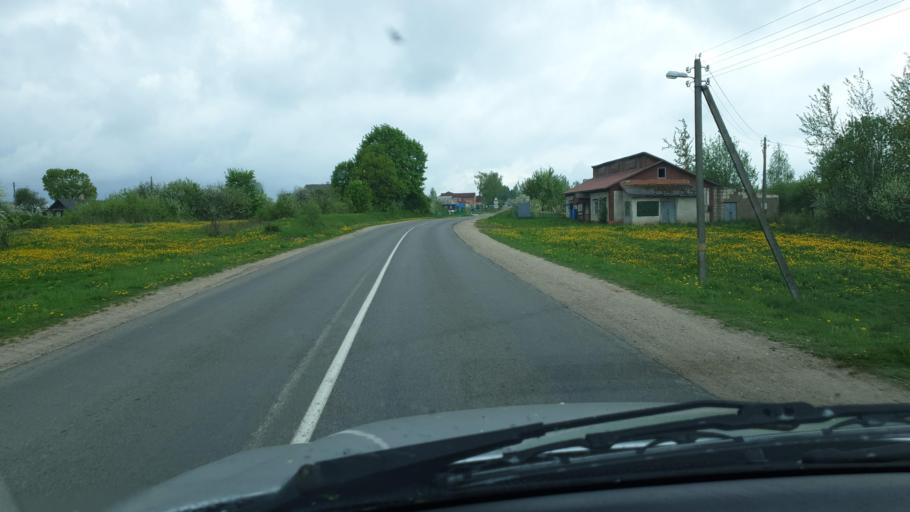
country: BY
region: Vitebsk
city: Lyepyel'
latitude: 54.8866
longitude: 28.6286
